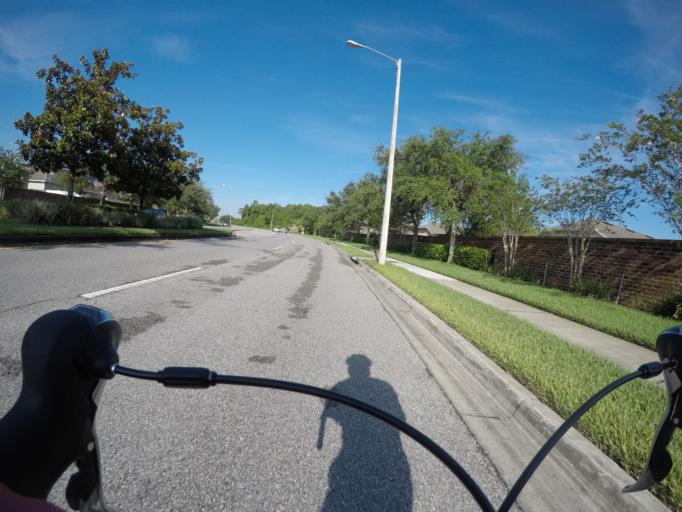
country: US
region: Florida
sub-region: Osceola County
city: Buenaventura Lakes
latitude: 28.3592
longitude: -81.3394
